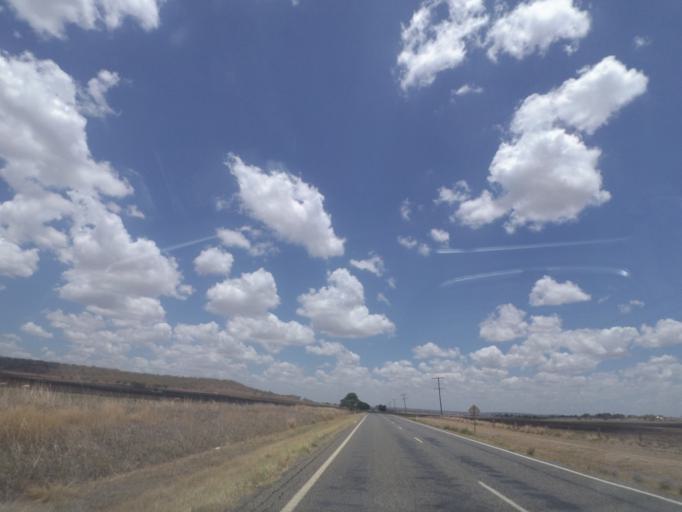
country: AU
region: Queensland
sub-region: Southern Downs
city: Warwick
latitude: -28.0053
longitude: 151.9912
